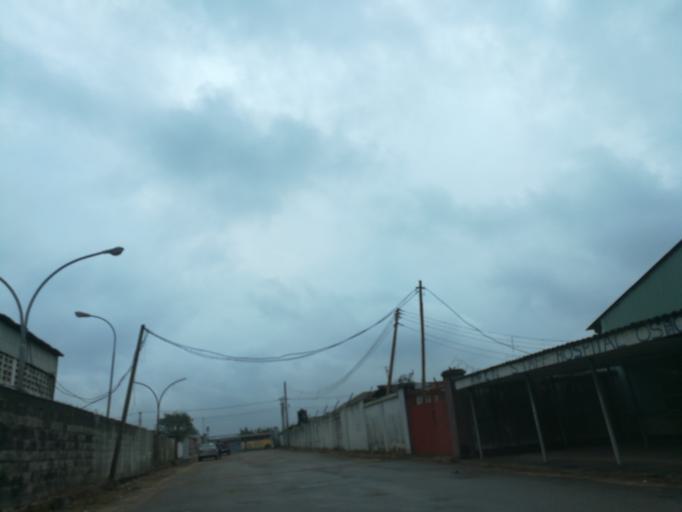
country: NG
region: Lagos
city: Oshodi
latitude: 6.5666
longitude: 3.3460
